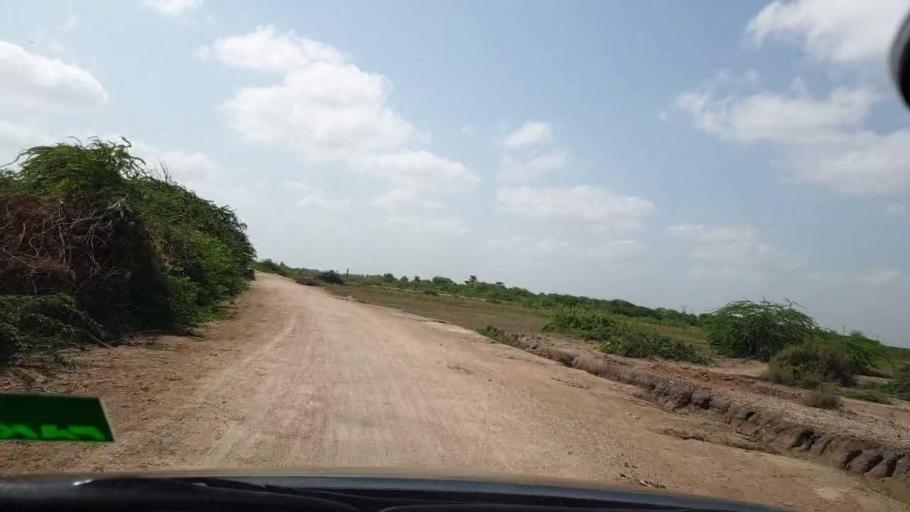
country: PK
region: Sindh
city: Kadhan
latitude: 24.5787
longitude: 69.1514
